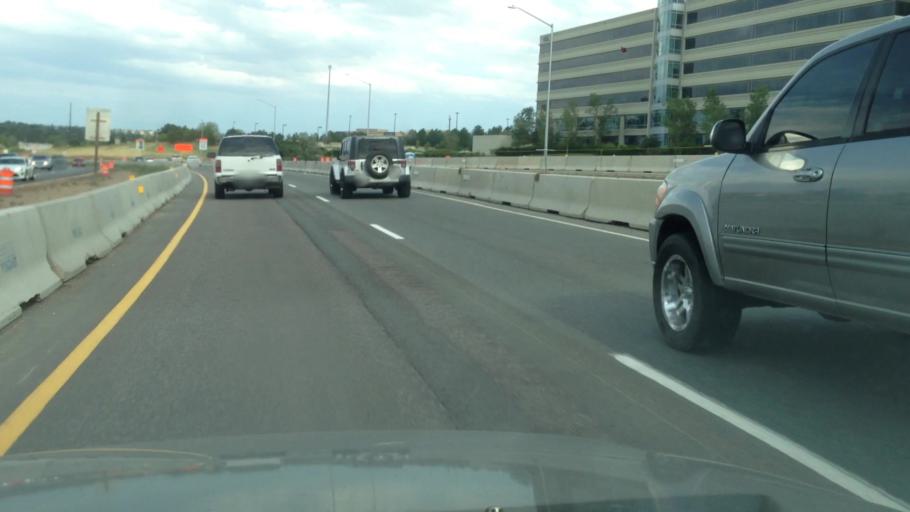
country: US
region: Colorado
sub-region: Douglas County
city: Highlands Ranch
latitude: 39.5588
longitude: -105.0039
